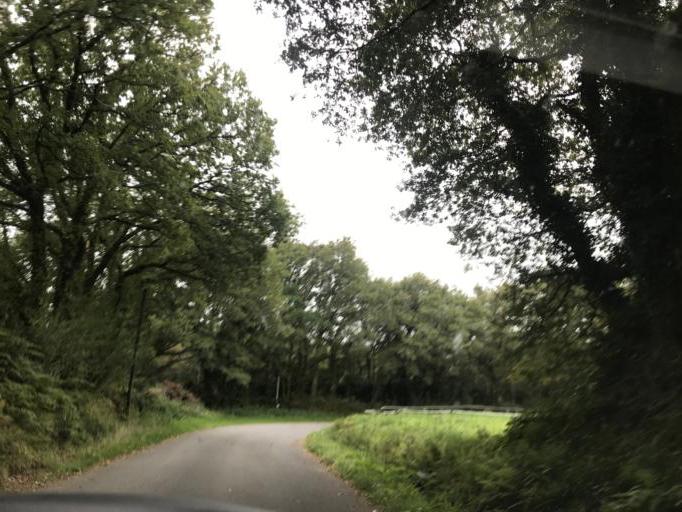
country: FR
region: Brittany
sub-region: Departement du Finistere
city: Plouneour-Menez
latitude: 48.3552
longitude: -3.8756
